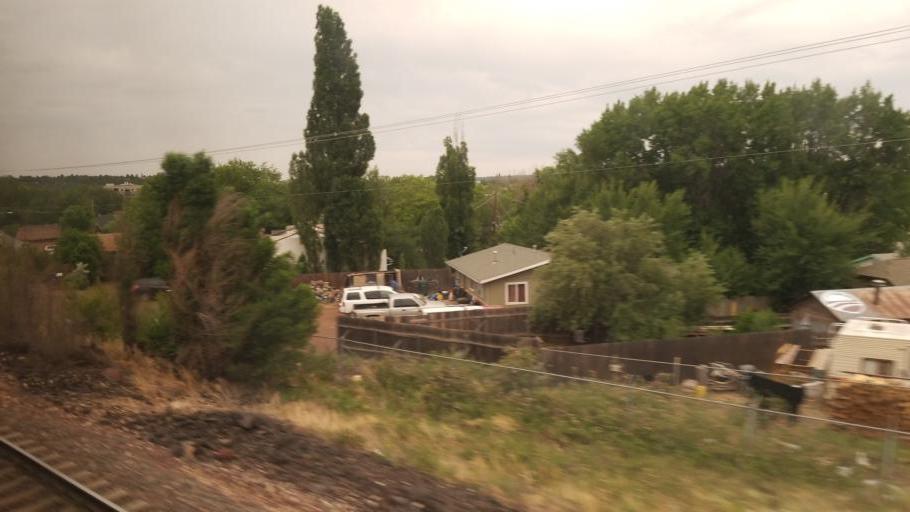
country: US
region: Arizona
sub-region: Coconino County
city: Flagstaff
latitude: 35.1972
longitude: -111.6591
